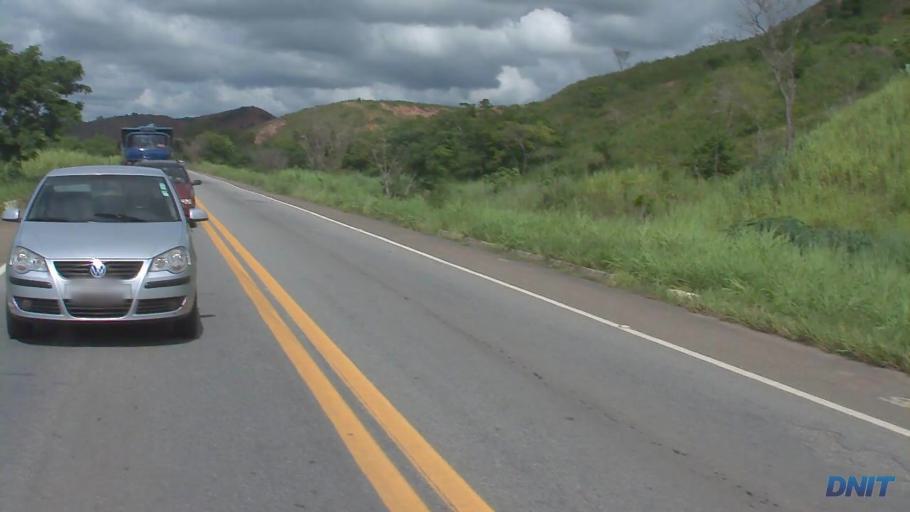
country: BR
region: Minas Gerais
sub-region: Belo Oriente
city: Belo Oriente
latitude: -19.1387
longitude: -42.2193
